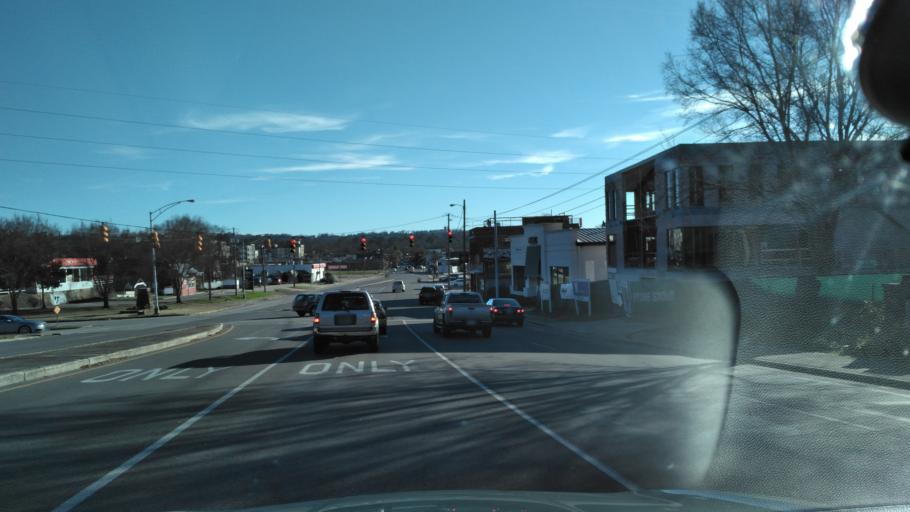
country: US
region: Alabama
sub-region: Jefferson County
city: Homewood
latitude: 33.4846
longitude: -86.7919
